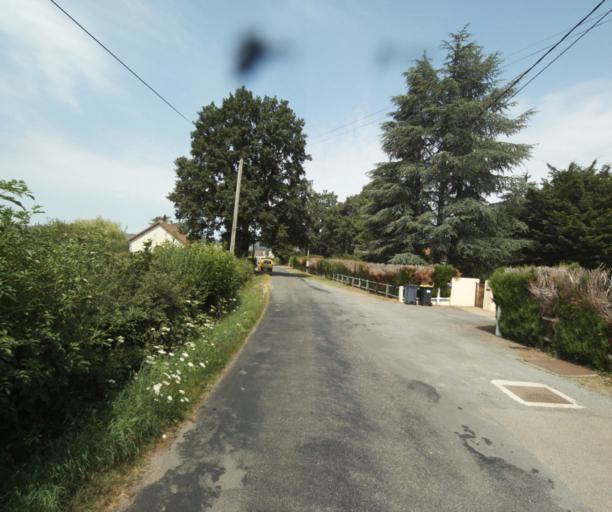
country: FR
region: Bourgogne
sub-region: Departement de Saone-et-Loire
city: Gueugnon
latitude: 46.5901
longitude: 4.0749
